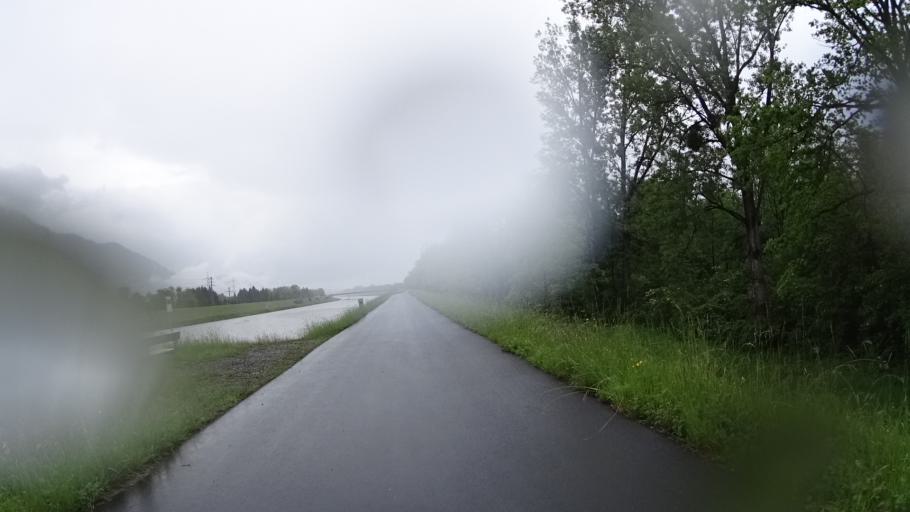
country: LI
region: Ruggell
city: Ruggell
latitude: 47.2336
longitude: 9.5130
